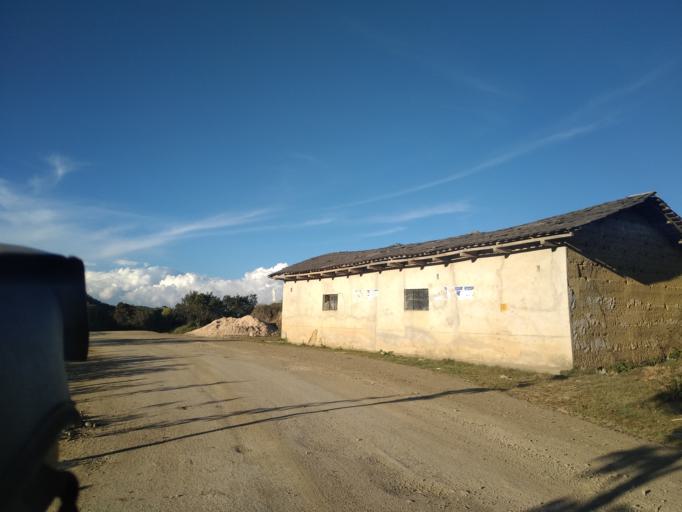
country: PE
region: Amazonas
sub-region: Provincia de Chachapoyas
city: Montevideo
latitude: -6.7176
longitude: -77.8658
